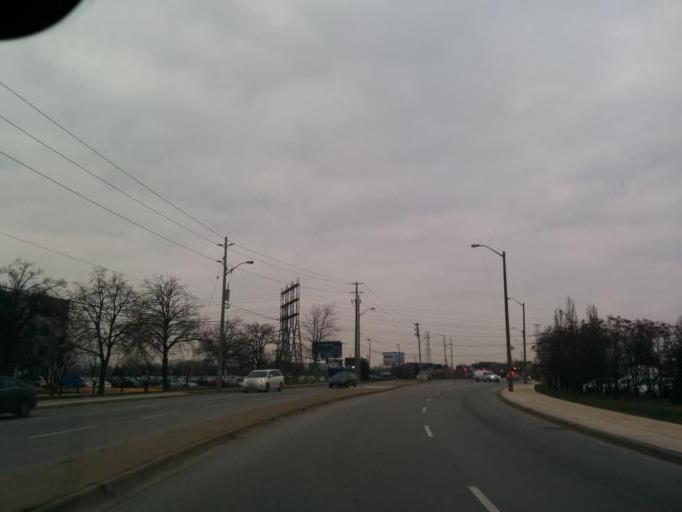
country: CA
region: Ontario
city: Etobicoke
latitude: 43.6099
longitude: -79.5609
